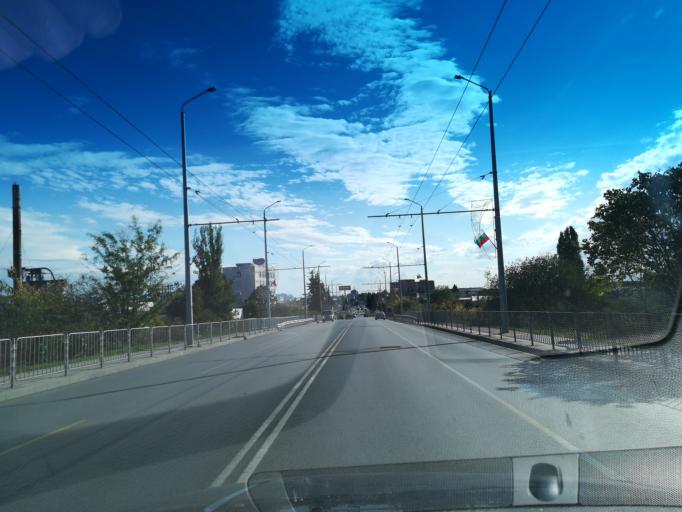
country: BG
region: Stara Zagora
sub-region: Obshtina Stara Zagora
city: Stara Zagora
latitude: 42.4191
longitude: 25.6372
